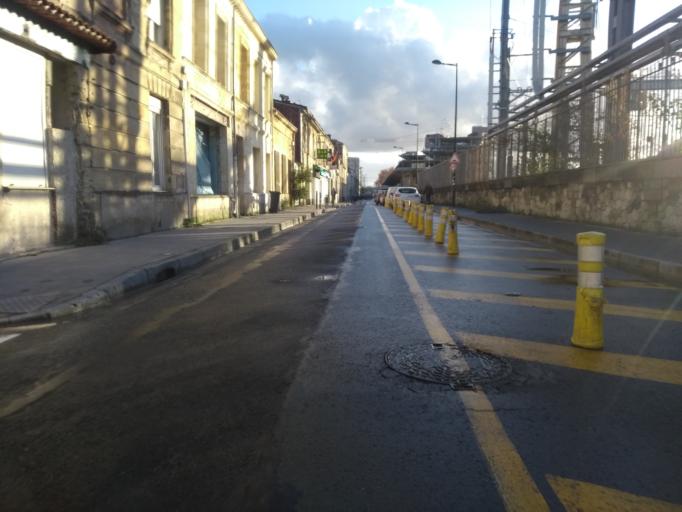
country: FR
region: Aquitaine
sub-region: Departement de la Gironde
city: Begles
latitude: 44.8263
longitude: -0.5546
